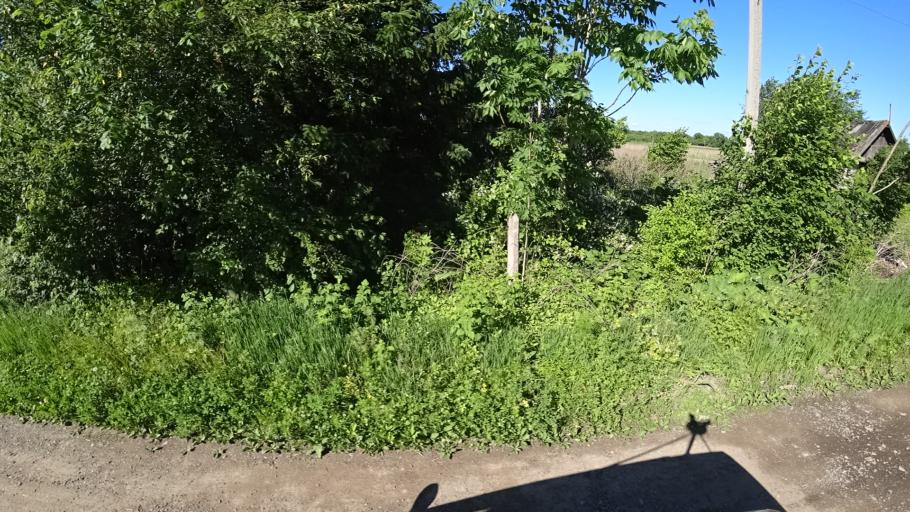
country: RU
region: Khabarovsk Krai
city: Khor
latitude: 47.8845
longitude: 135.0195
